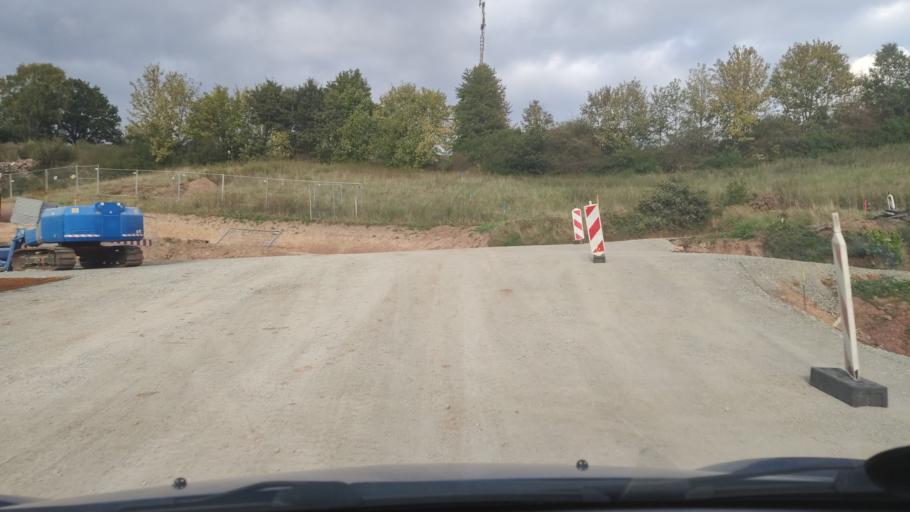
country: DE
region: Lower Saxony
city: Uslar
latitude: 51.6585
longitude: 9.7141
